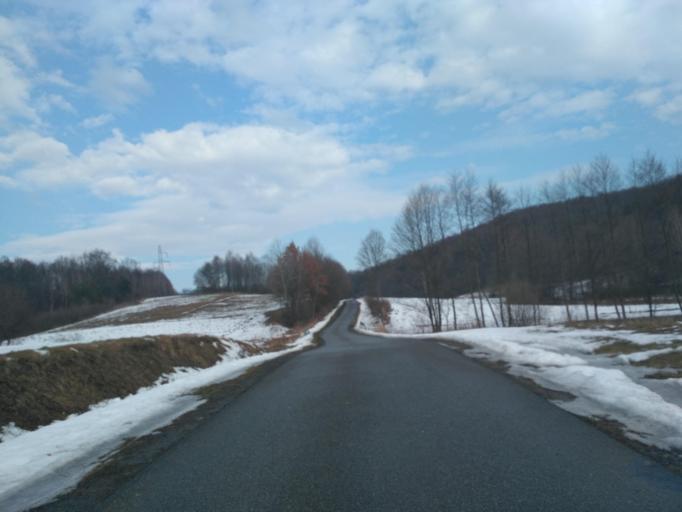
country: PL
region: Subcarpathian Voivodeship
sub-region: Powiat brzozowski
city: Niebocko
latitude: 49.6446
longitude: 22.1301
